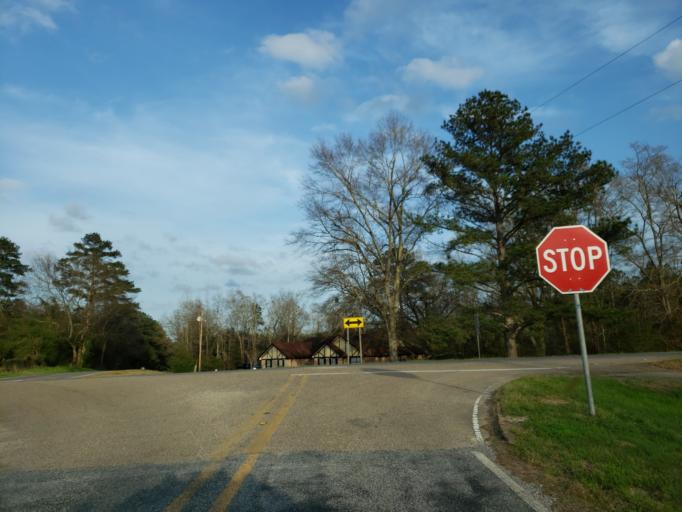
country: US
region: Mississippi
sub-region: Clarke County
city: Stonewall
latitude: 32.1734
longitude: -88.6793
